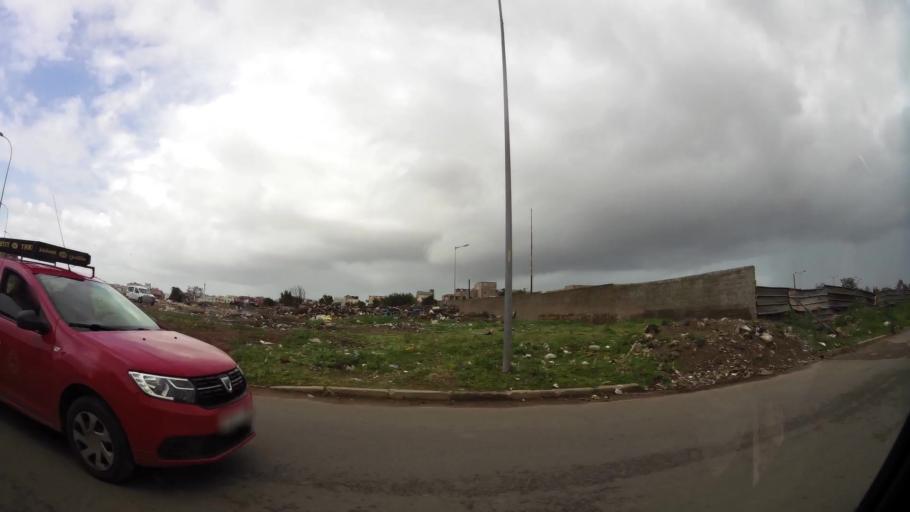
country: MA
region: Grand Casablanca
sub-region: Casablanca
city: Casablanca
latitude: 33.5697
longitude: -7.6893
